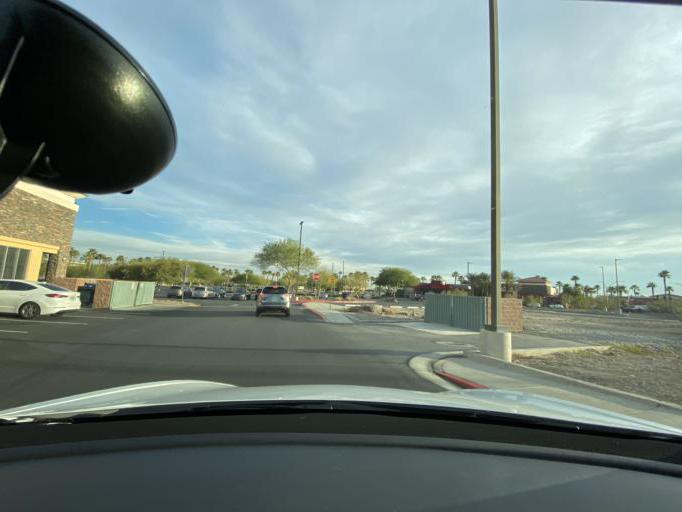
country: US
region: Nevada
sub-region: Clark County
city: Las Vegas
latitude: 36.2724
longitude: -115.2670
